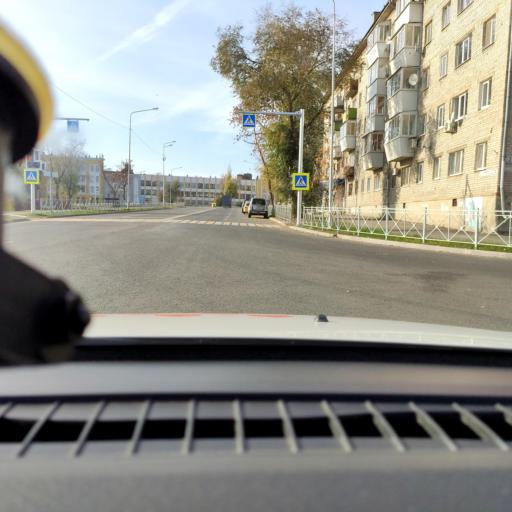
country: RU
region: Samara
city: Rozhdestveno
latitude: 53.1788
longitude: 50.0833
